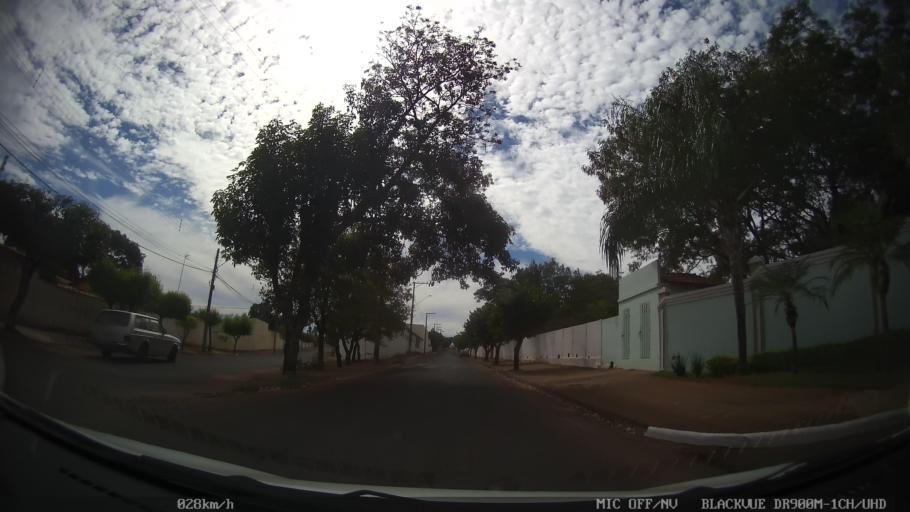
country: BR
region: Sao Paulo
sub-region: Catanduva
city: Catanduva
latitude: -21.1545
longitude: -48.9717
